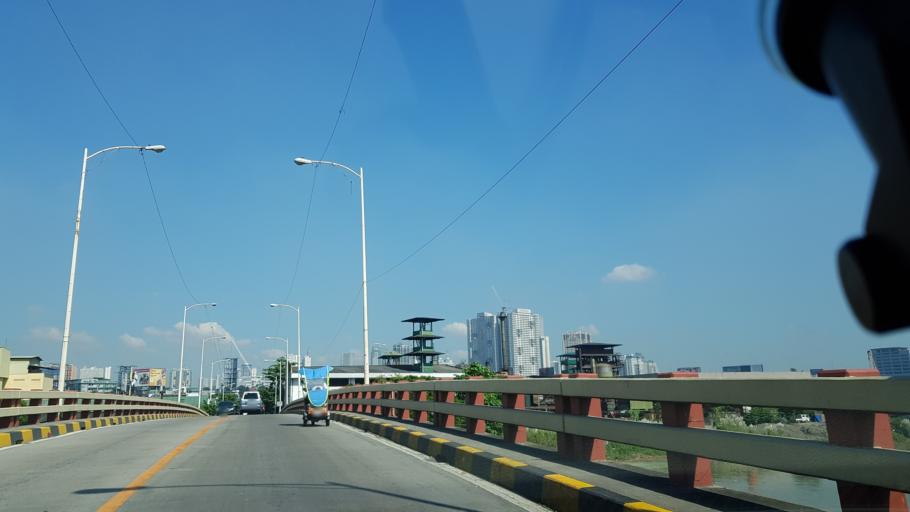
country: PH
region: Calabarzon
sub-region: Province of Rizal
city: Pateros
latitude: 14.5597
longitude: 121.0726
